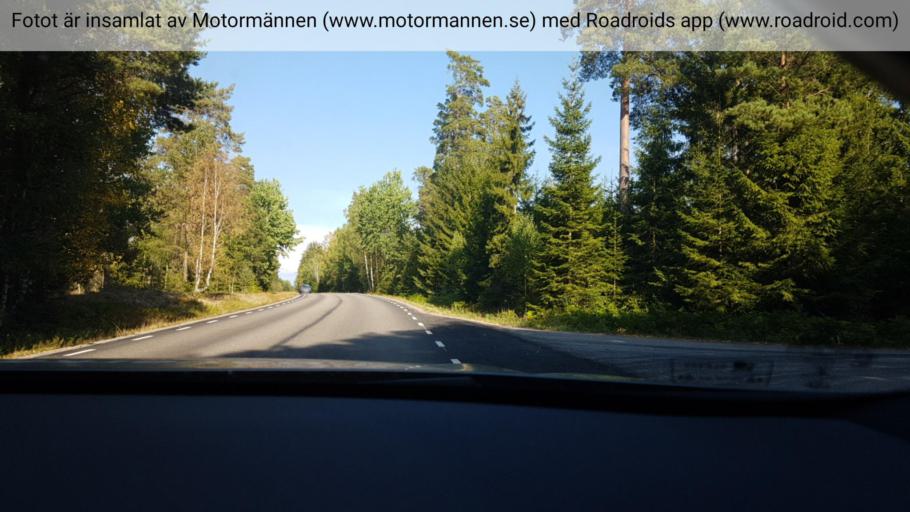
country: SE
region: Vaestra Goetaland
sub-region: Gotene Kommun
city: Goetene
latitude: 58.6205
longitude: 13.5852
